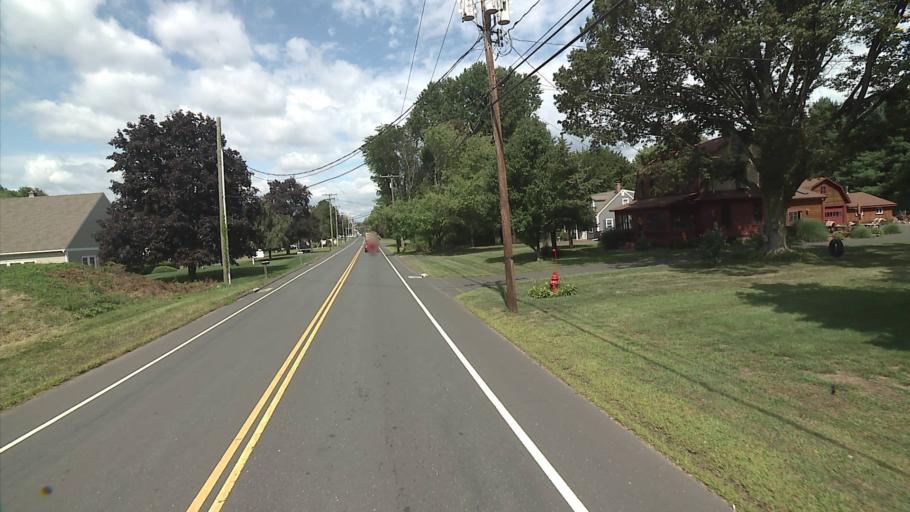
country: US
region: Connecticut
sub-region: Hartford County
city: Salmon Brook
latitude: 41.9496
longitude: -72.7839
